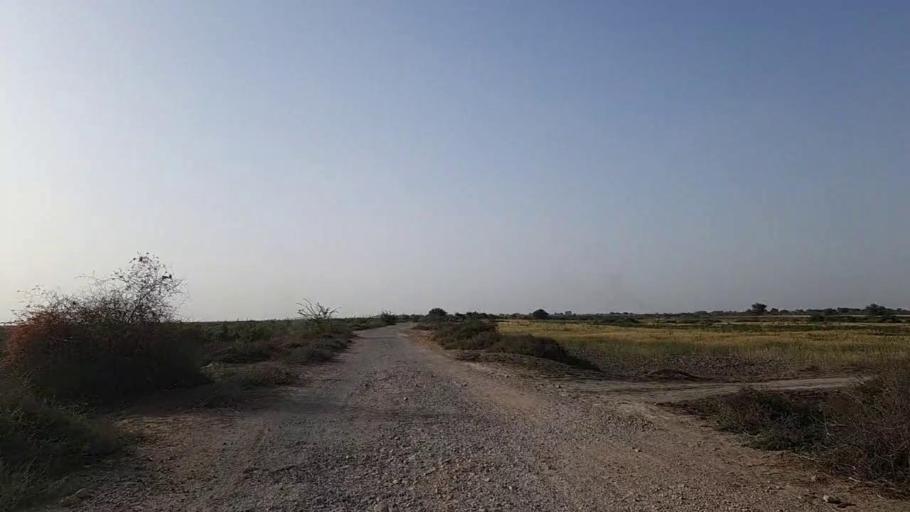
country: PK
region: Sindh
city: Jati
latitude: 24.3031
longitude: 68.1689
